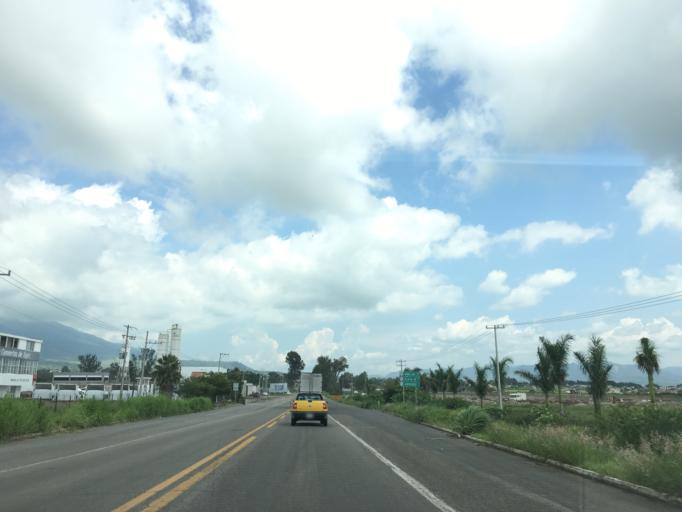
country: MX
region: Nayarit
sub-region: Tepic
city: La Corregidora
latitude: 21.4609
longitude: -104.8288
